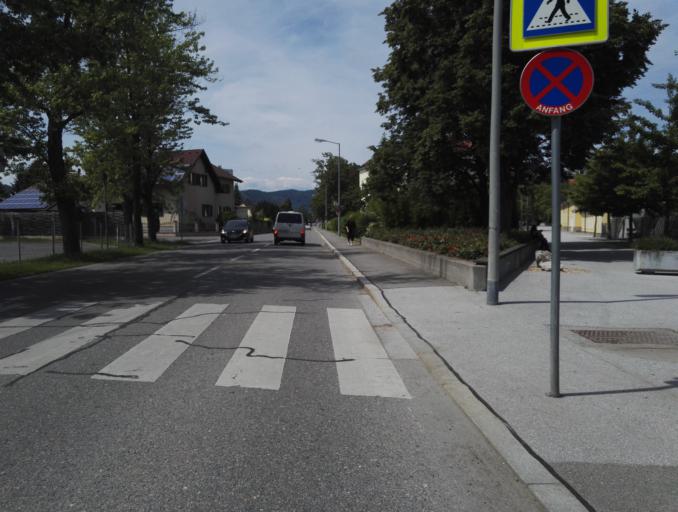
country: AT
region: Styria
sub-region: Graz Stadt
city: Wetzelsdorf
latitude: 47.0358
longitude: 15.4176
